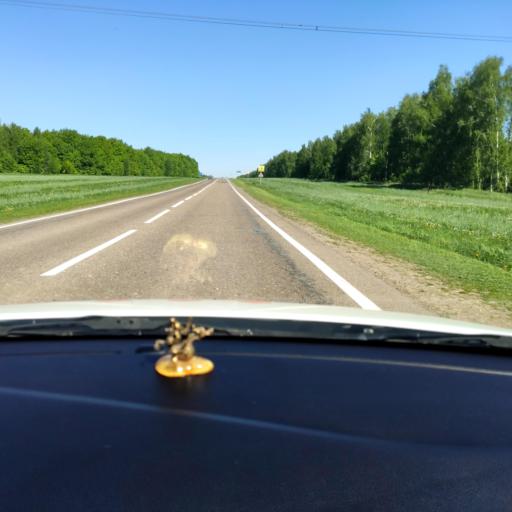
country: RU
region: Tatarstan
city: Vysokaya Gora
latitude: 56.0772
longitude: 49.1886
